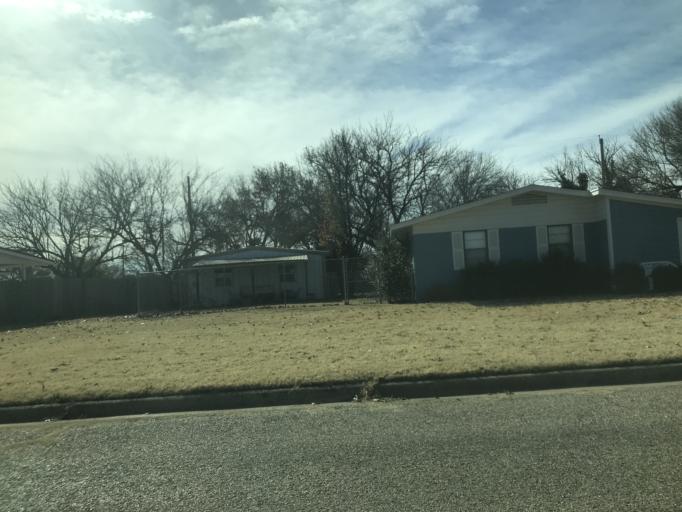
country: US
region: Texas
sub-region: Taylor County
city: Abilene
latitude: 32.4783
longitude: -99.7134
